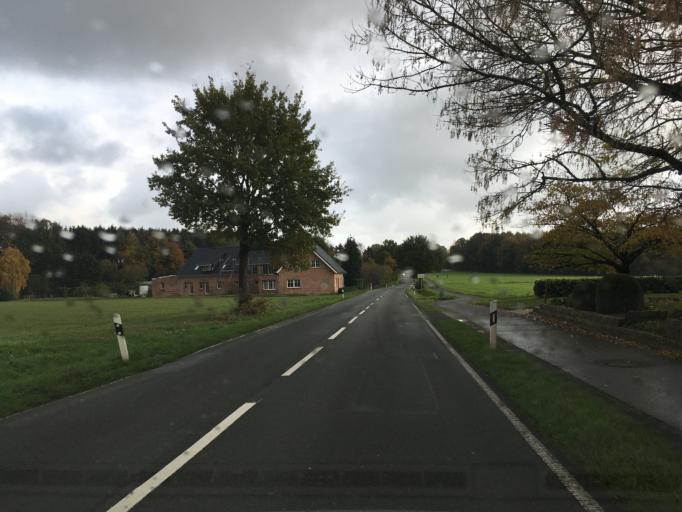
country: DE
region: North Rhine-Westphalia
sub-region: Regierungsbezirk Munster
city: Klein Reken
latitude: 51.8291
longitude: 7.0115
